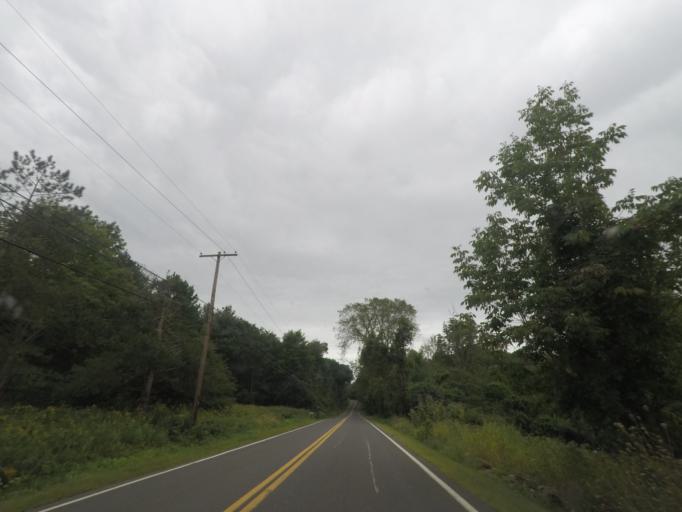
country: US
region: New York
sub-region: Rensselaer County
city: Nassau
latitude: 42.4549
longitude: -73.5739
